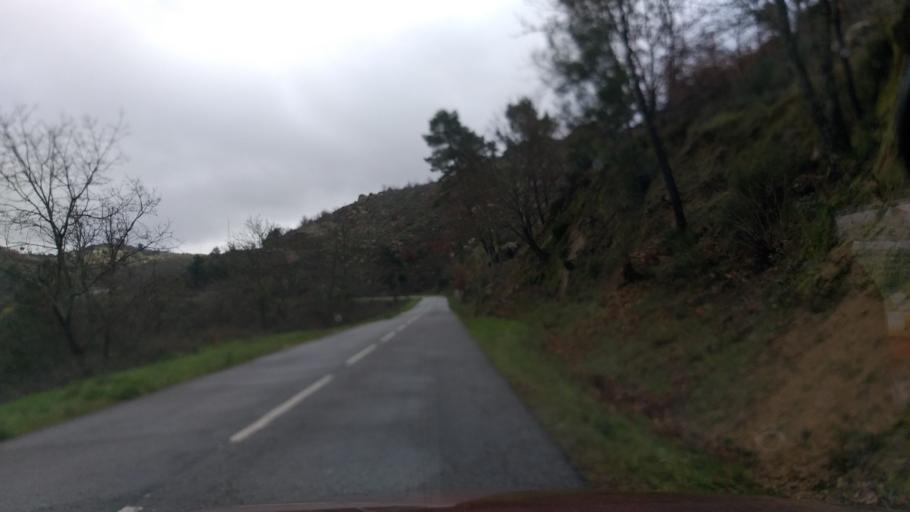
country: PT
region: Guarda
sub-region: Celorico da Beira
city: Celorico da Beira
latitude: 40.7100
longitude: -7.4238
